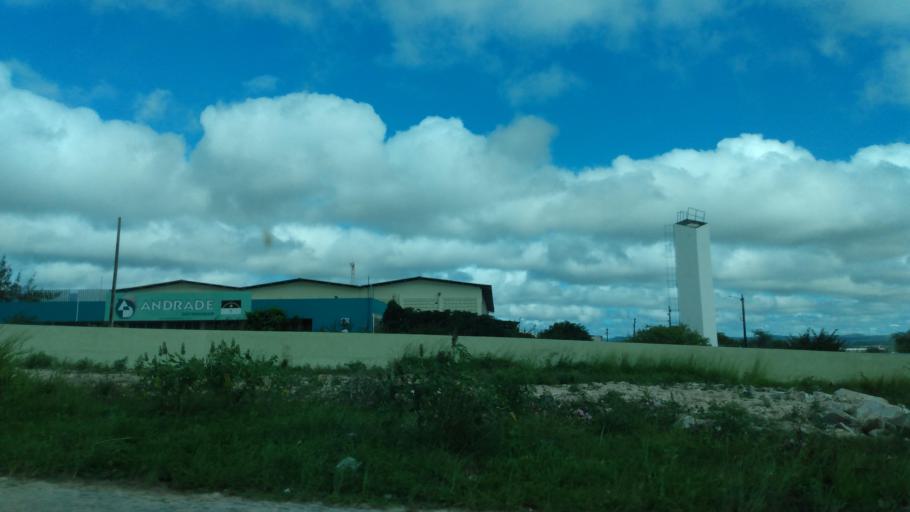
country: BR
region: Pernambuco
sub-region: Caruaru
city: Caruaru
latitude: -8.3074
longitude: -35.9898
